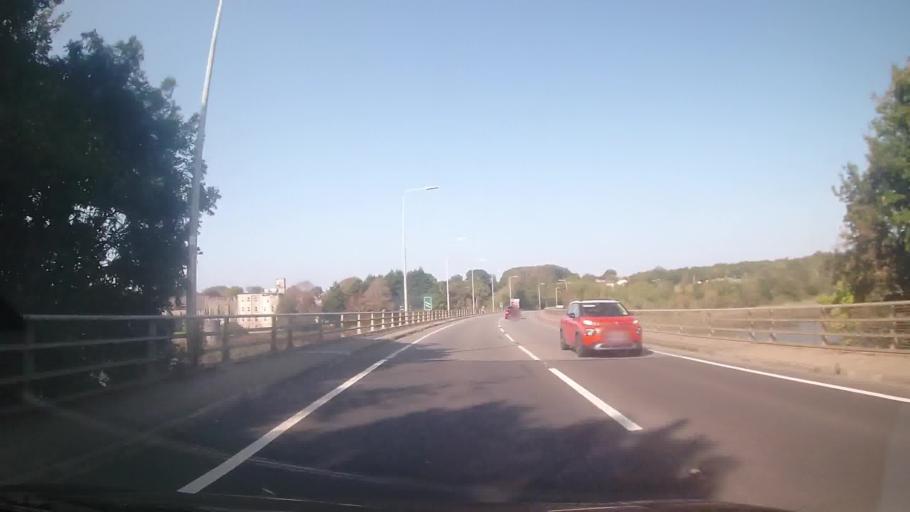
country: GB
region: Wales
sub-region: County of Ceredigion
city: Cardigan
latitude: 52.0806
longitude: -4.6544
